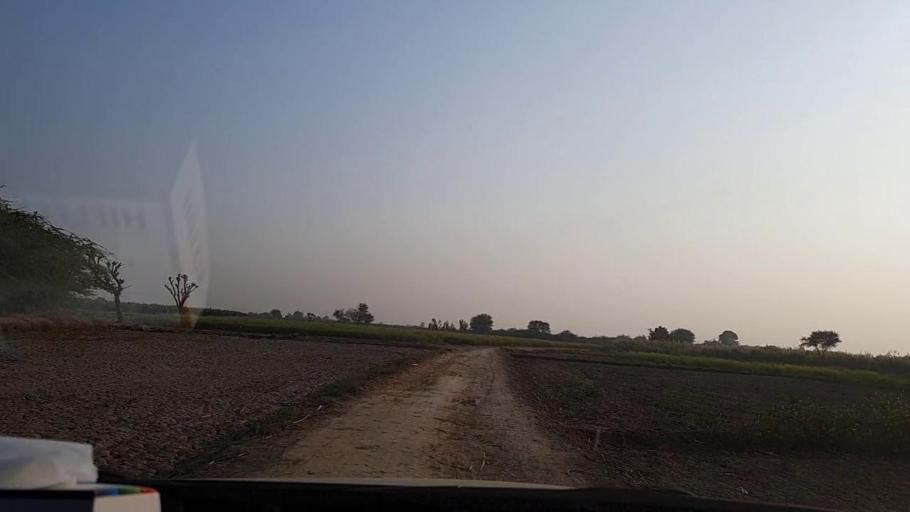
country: PK
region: Sindh
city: Tando Ghulam Ali
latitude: 25.1999
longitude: 68.9190
